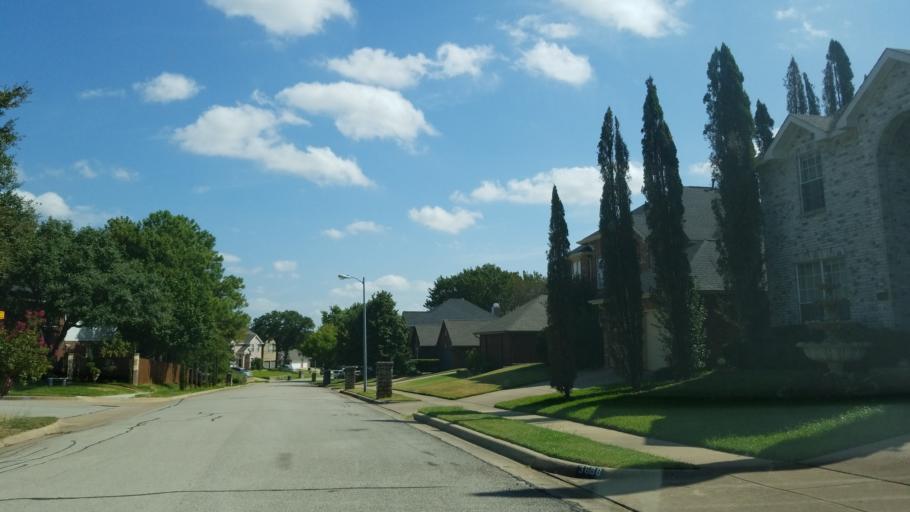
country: US
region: Texas
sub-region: Tarrant County
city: Euless
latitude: 32.8580
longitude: -97.1039
